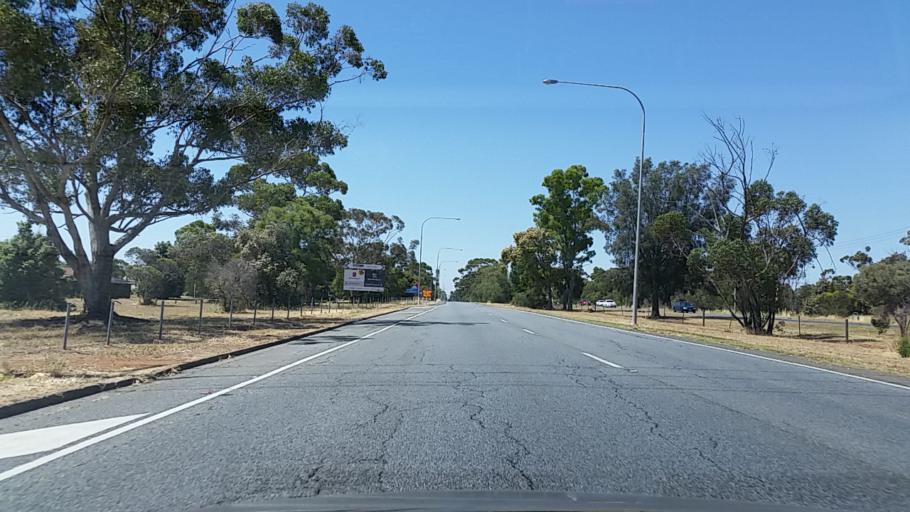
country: AU
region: South Australia
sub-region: Playford
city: Smithfield
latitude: -34.6952
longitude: 138.6859
